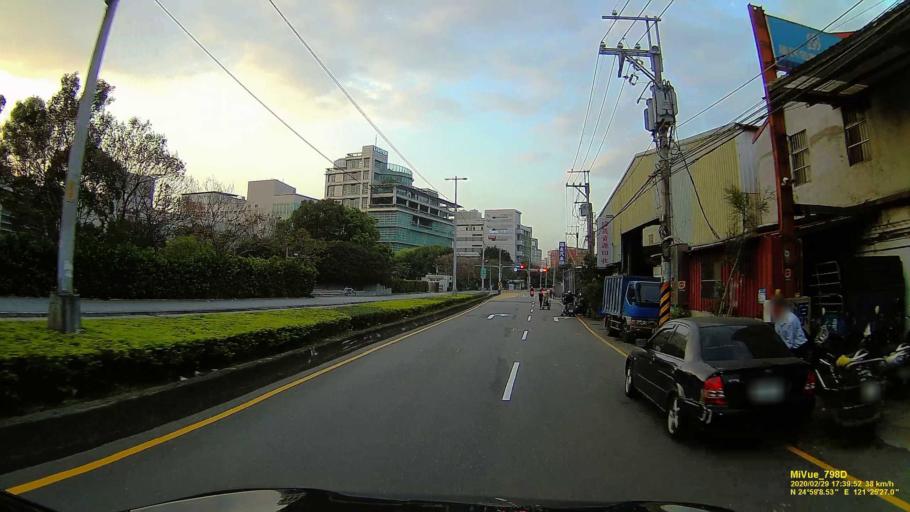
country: TW
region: Taipei
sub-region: Taipei
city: Banqiao
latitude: 24.9860
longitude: 121.4242
